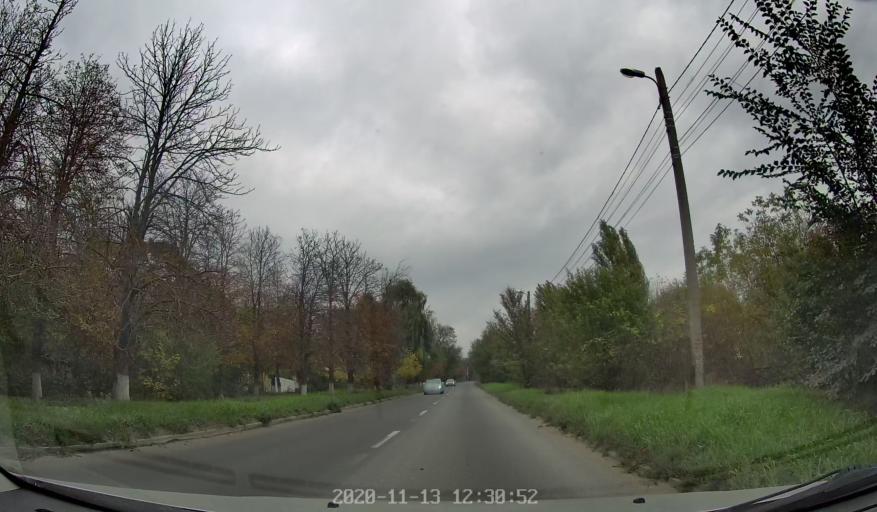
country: MD
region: Chisinau
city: Chisinau
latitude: 46.9736
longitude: 28.8348
